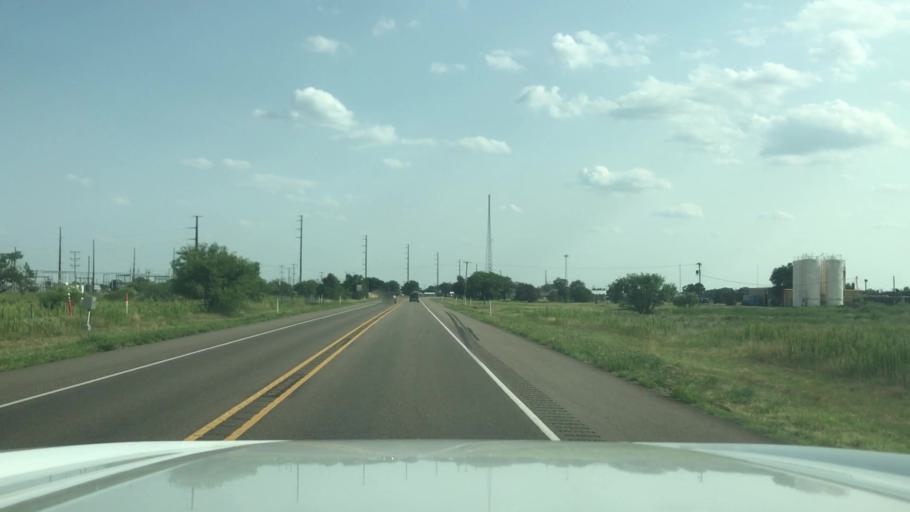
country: US
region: Texas
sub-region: Hartley County
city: Channing
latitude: 35.6924
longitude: -102.3283
